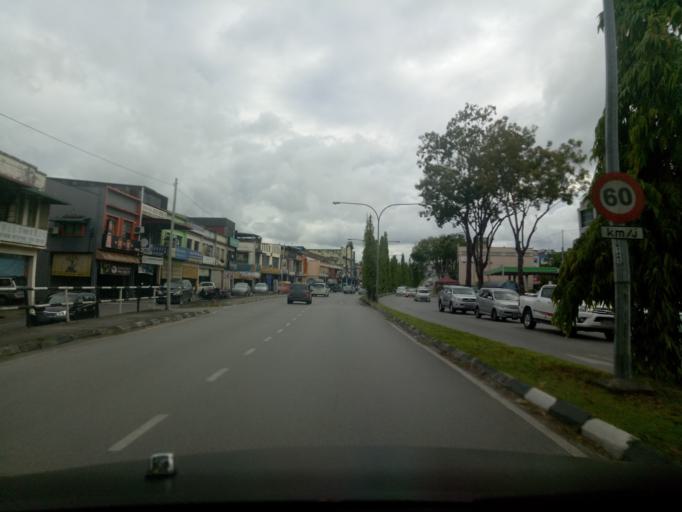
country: MY
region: Sarawak
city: Kuching
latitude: 1.5501
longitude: 110.3800
